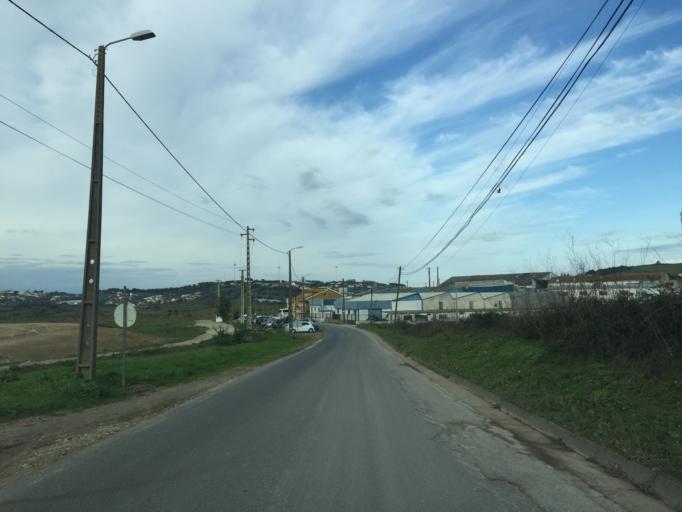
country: PT
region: Lisbon
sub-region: Odivelas
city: Canecas
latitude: 38.8253
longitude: -9.2443
